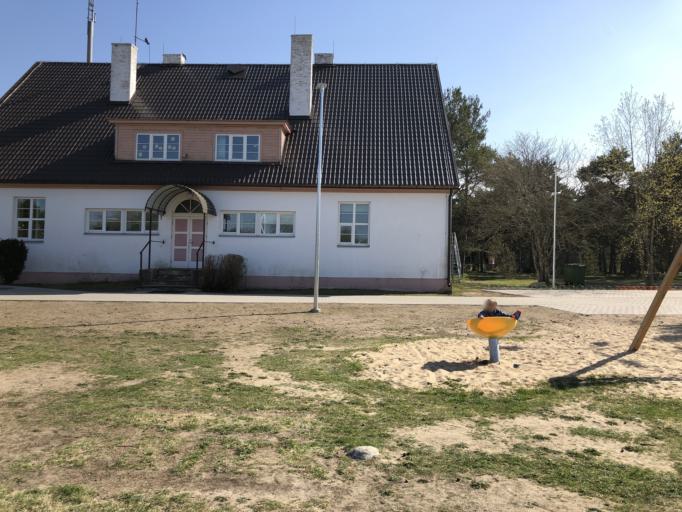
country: EE
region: Harju
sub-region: Maardu linn
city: Maardu
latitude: 59.5292
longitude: 25.1576
